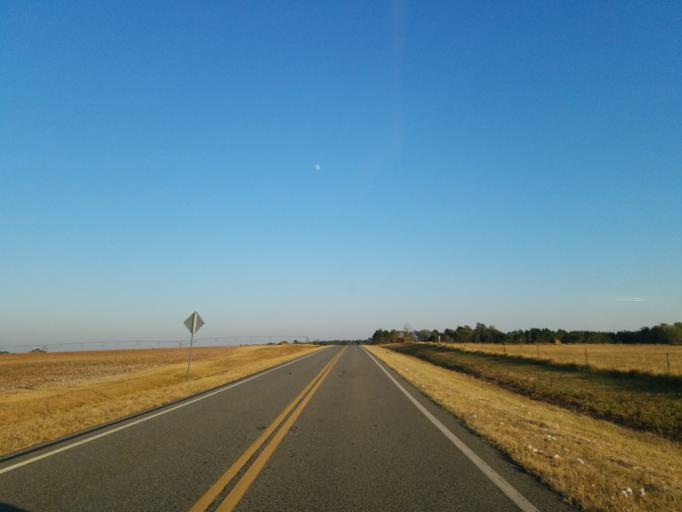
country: US
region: Georgia
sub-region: Turner County
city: Ashburn
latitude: 31.8594
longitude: -83.5978
